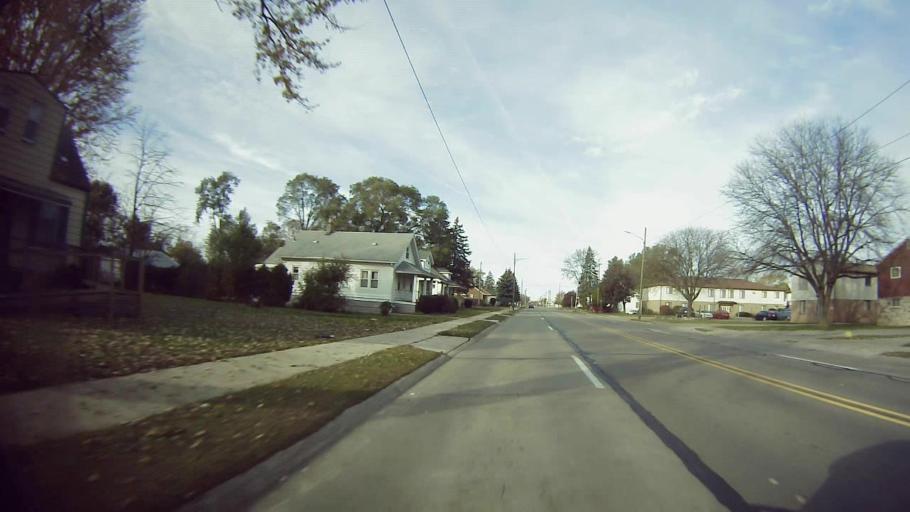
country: US
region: Michigan
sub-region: Macomb County
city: Eastpointe
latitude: 42.4796
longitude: -82.9530
